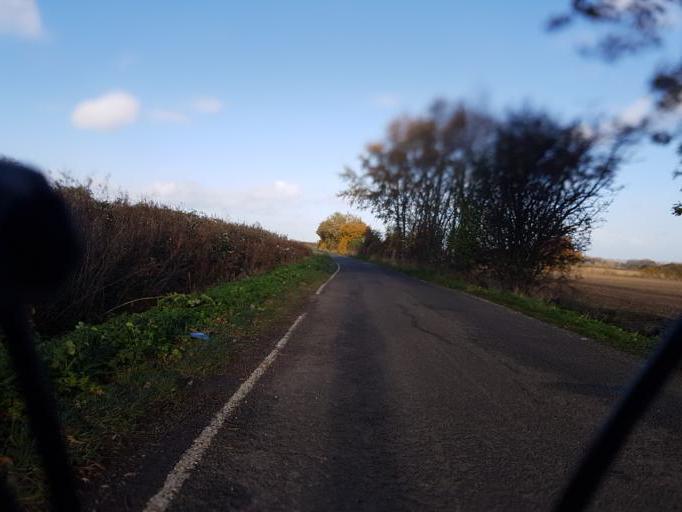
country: GB
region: England
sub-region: Kent
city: Newington
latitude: 51.3647
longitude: 0.6901
